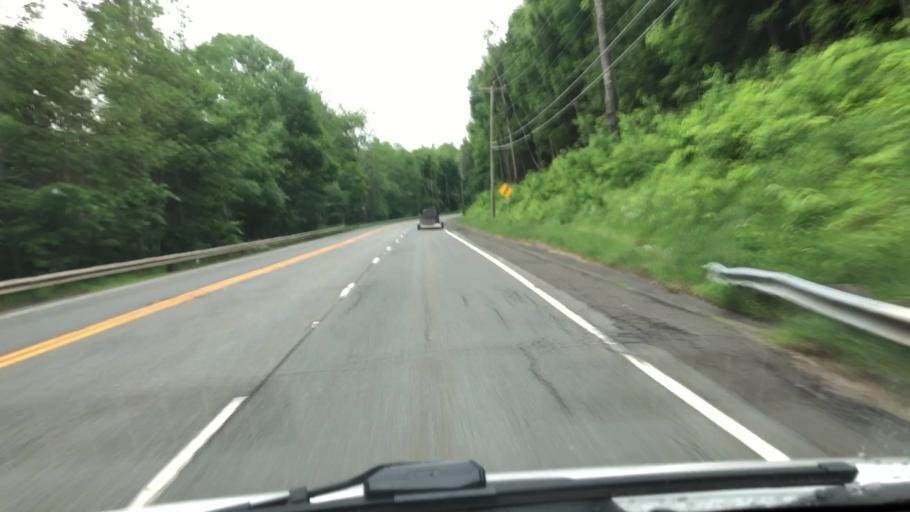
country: US
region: Massachusetts
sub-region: Berkshire County
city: Dalton
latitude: 42.4936
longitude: -73.1156
